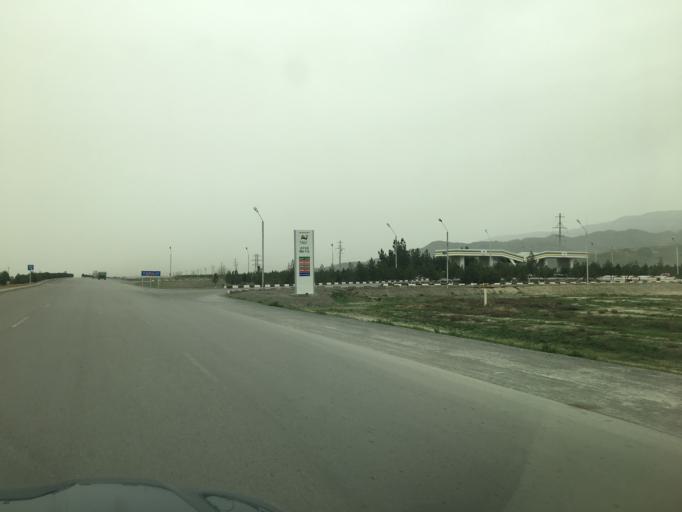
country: TM
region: Ahal
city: Baharly
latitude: 38.2760
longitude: 57.6855
